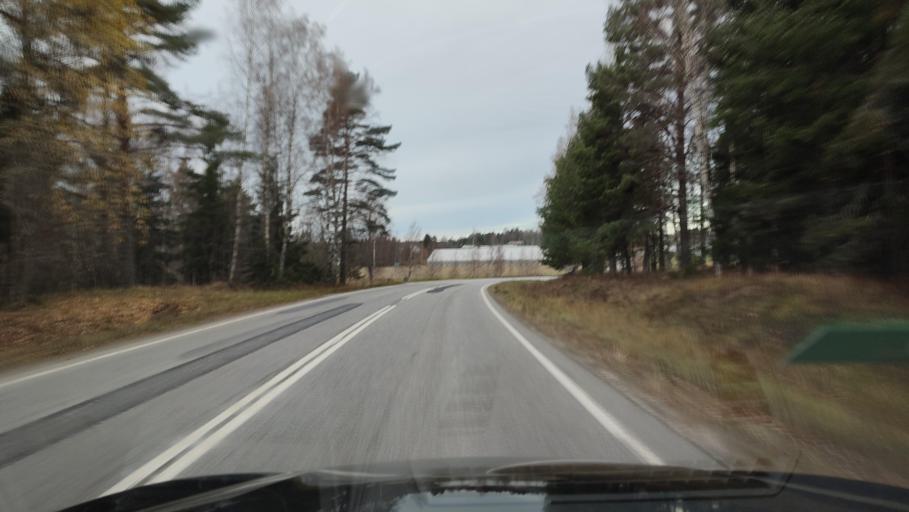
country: FI
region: Ostrobothnia
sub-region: Sydosterbotten
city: Naerpes
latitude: 62.4026
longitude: 21.3563
